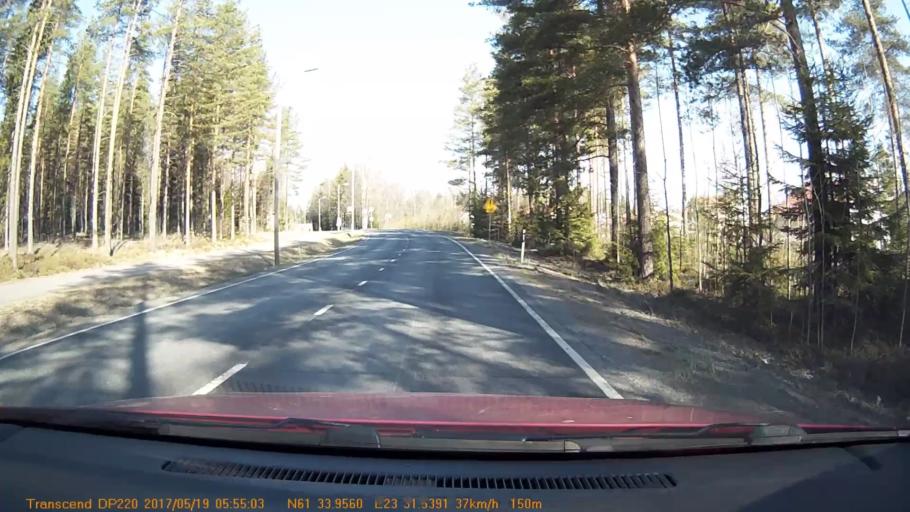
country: FI
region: Pirkanmaa
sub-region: Tampere
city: Yloejaervi
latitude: 61.5658
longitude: 23.5260
